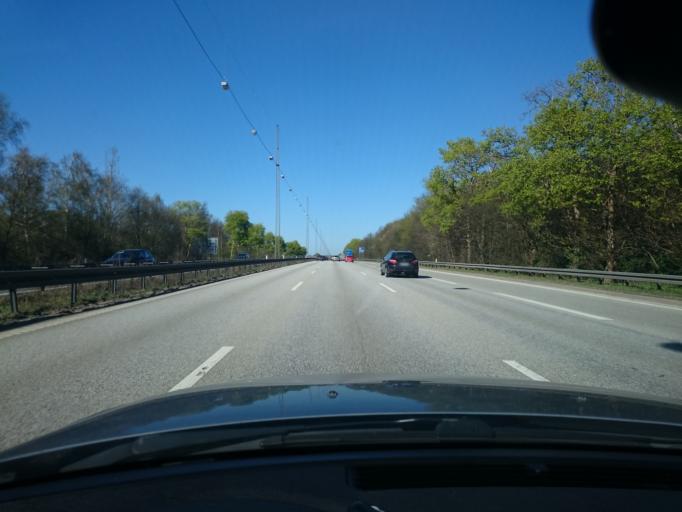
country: DK
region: Capital Region
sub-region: Lyngby-Tarbaek Kommune
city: Kongens Lyngby
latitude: 55.7812
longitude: 12.5267
